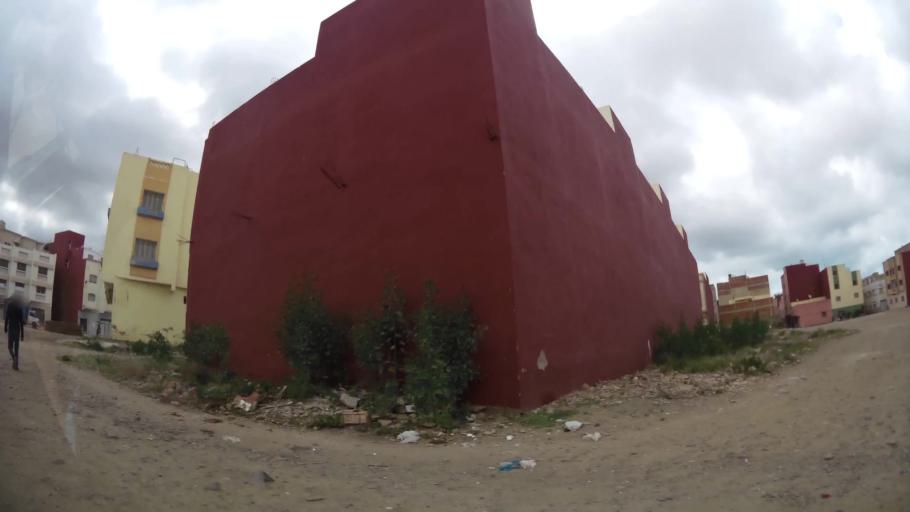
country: MA
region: Oriental
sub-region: Nador
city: Nador
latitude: 35.1666
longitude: -2.9409
